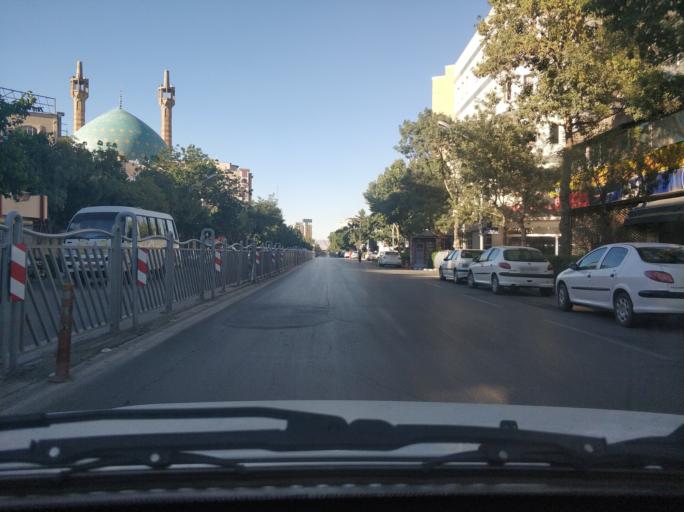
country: IR
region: Razavi Khorasan
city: Mashhad
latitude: 36.2914
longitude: 59.6068
